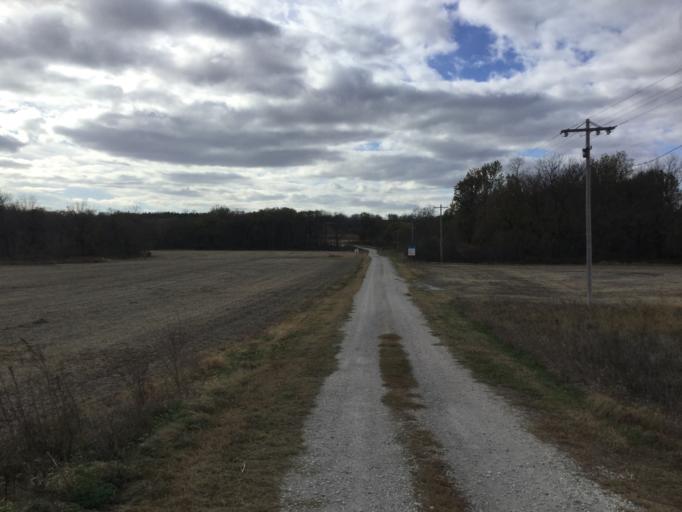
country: US
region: Kansas
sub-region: Pottawatomie County
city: Westmoreland
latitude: 39.6678
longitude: -96.3593
